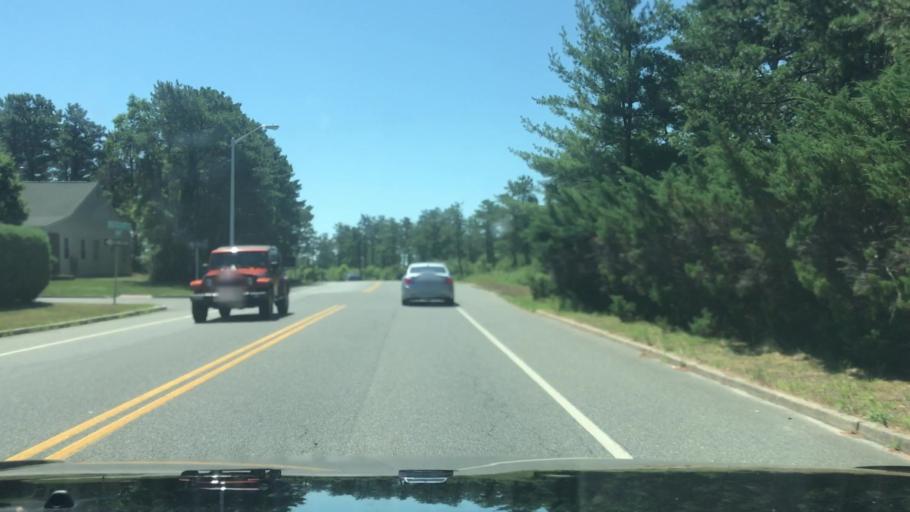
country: US
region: New Jersey
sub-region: Ocean County
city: Holiday City South
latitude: 39.9426
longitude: -74.2386
